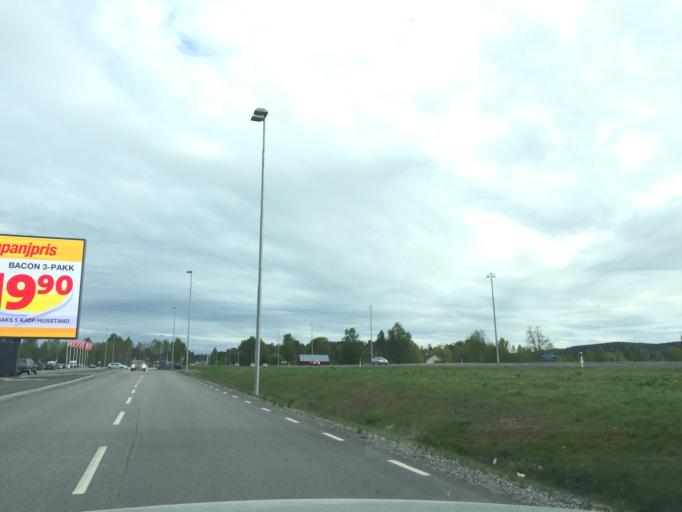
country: SE
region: Vaermland
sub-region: Eda Kommun
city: Charlottenberg
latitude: 59.8869
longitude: 12.2832
